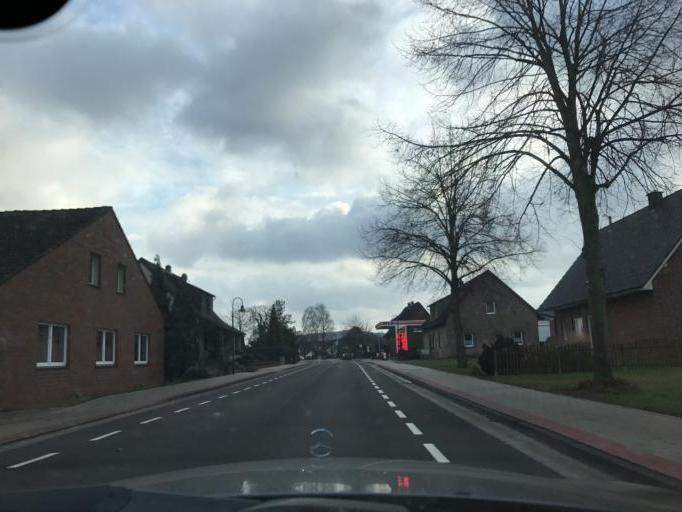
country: DE
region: Lower Saxony
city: Hasbergen
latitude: 52.2042
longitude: 7.9291
